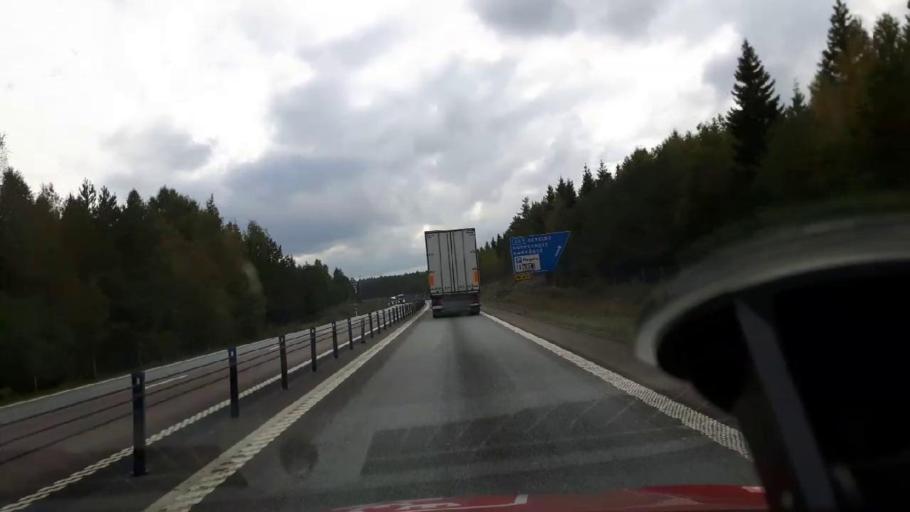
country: SE
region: Gaevleborg
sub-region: Gavle Kommun
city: Norrsundet
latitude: 60.9083
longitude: 17.0145
